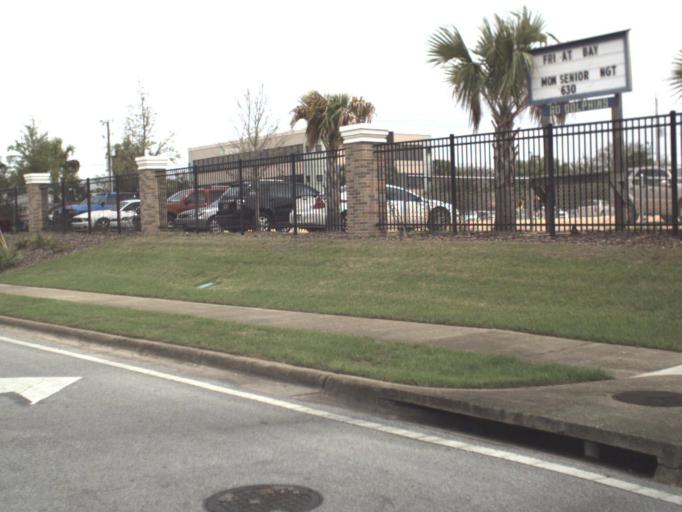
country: US
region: Florida
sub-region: Santa Rosa County
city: Gulf Breeze
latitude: 30.3633
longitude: -87.1690
